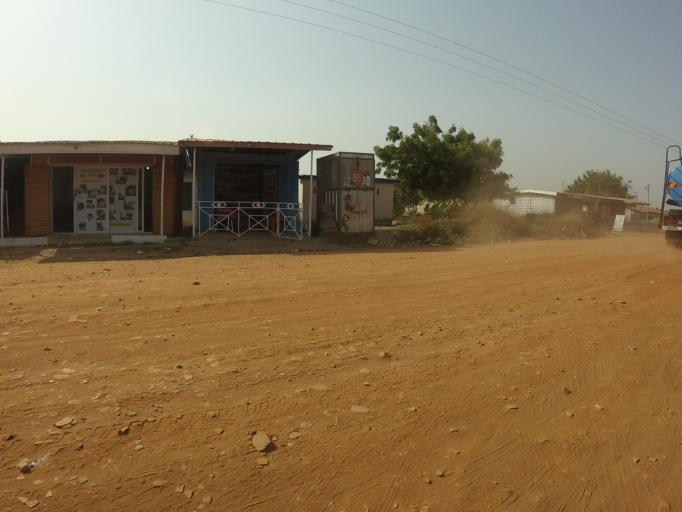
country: GH
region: Greater Accra
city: Tema
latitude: 5.7048
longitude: 0.0574
